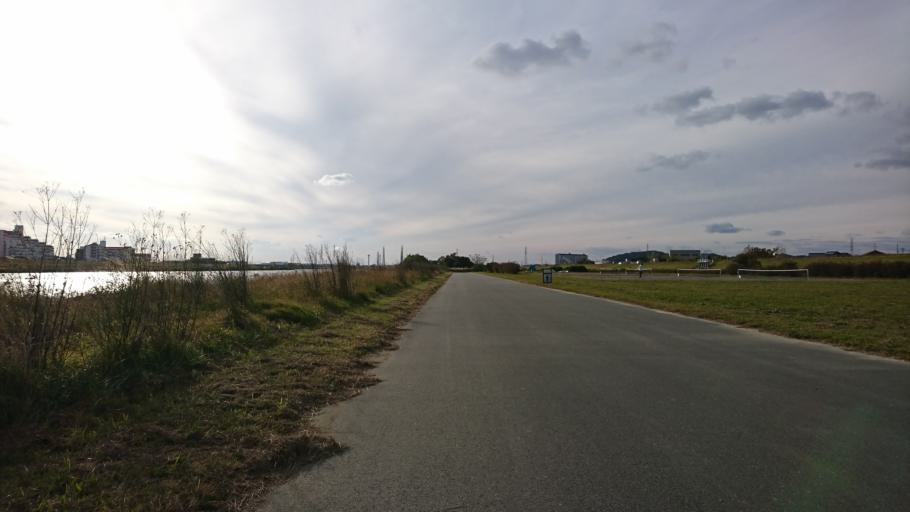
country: JP
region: Hyogo
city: Kakogawacho-honmachi
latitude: 34.7730
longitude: 134.8255
